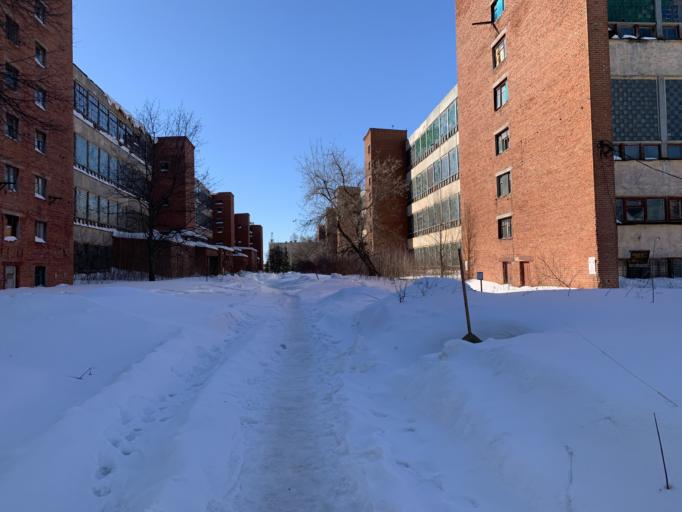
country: RU
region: Chuvashia
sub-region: Cheboksarskiy Rayon
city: Cheboksary
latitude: 56.1415
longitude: 47.2784
